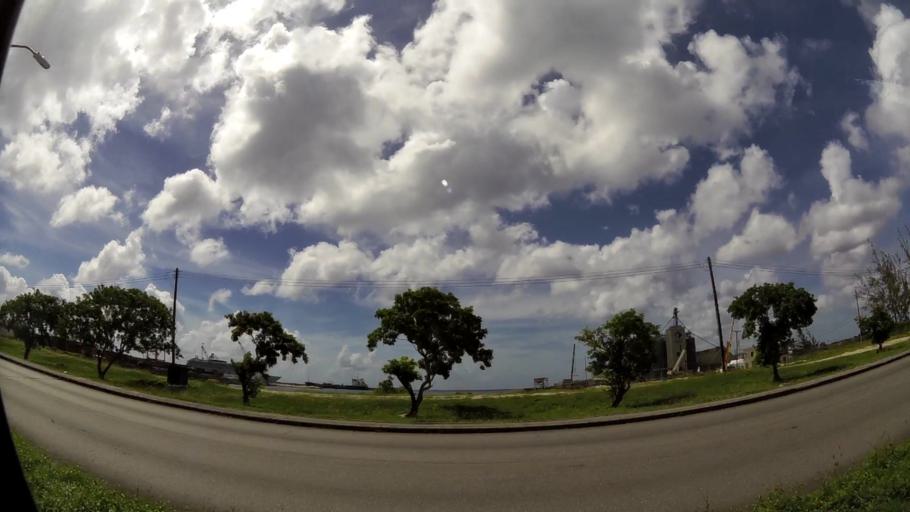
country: BB
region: Saint Michael
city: Bridgetown
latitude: 13.1105
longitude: -59.6266
